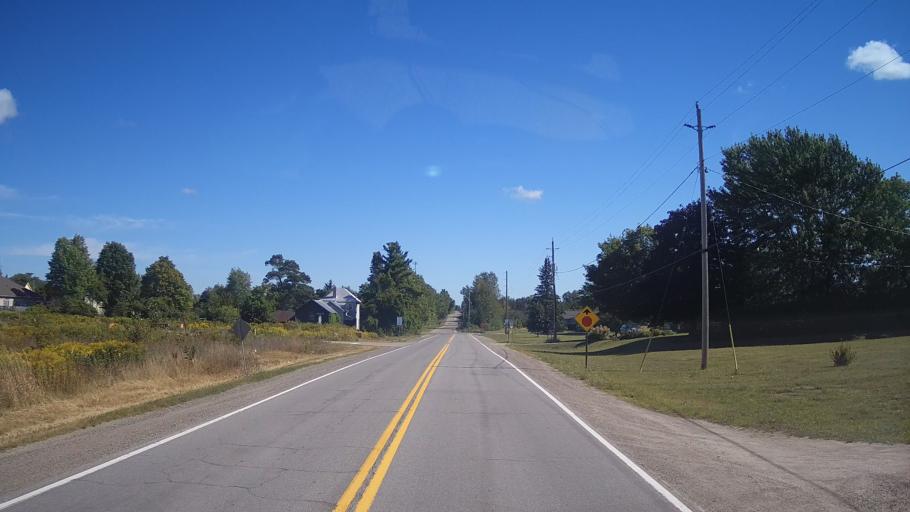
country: CA
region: Ontario
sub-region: Lanark County
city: Smiths Falls
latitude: 44.9068
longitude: -75.8363
